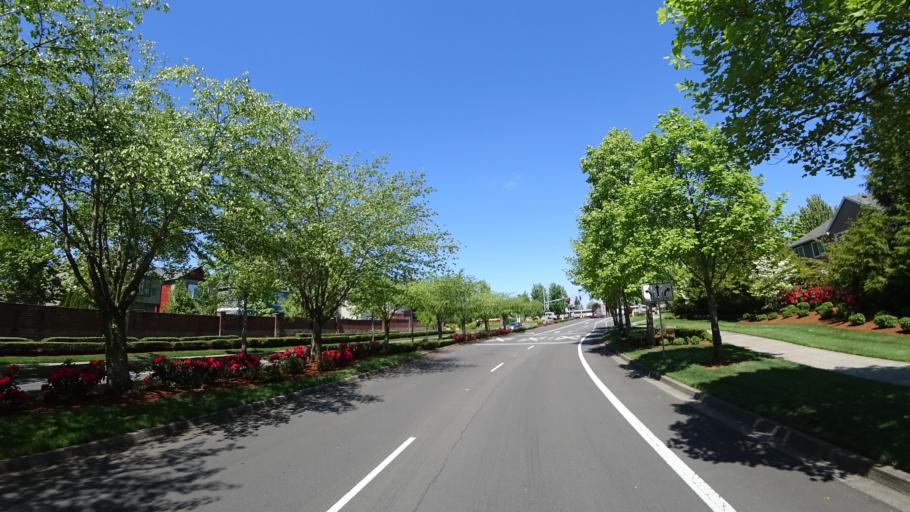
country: US
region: Oregon
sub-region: Washington County
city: Hillsboro
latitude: 45.5107
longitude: -122.9739
